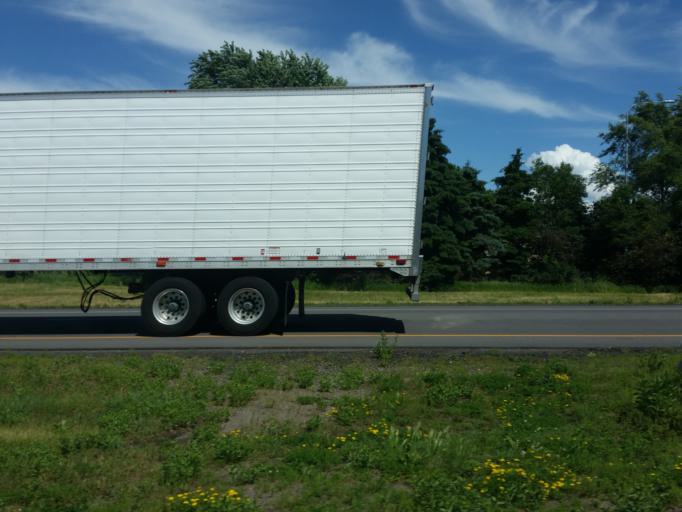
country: US
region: Minnesota
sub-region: Stearns County
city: Waite Park
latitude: 45.5697
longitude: -94.2059
